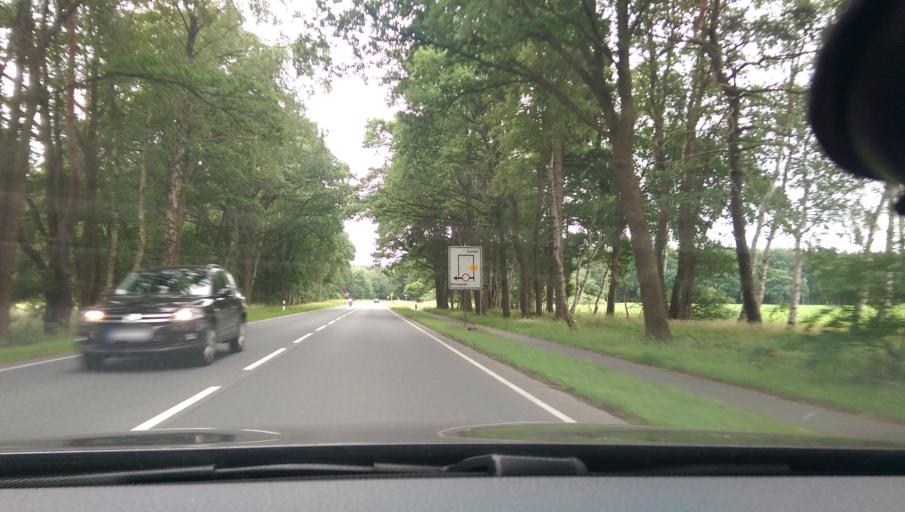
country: DE
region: Lower Saxony
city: Ahausen
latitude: 53.0612
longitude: 9.3438
